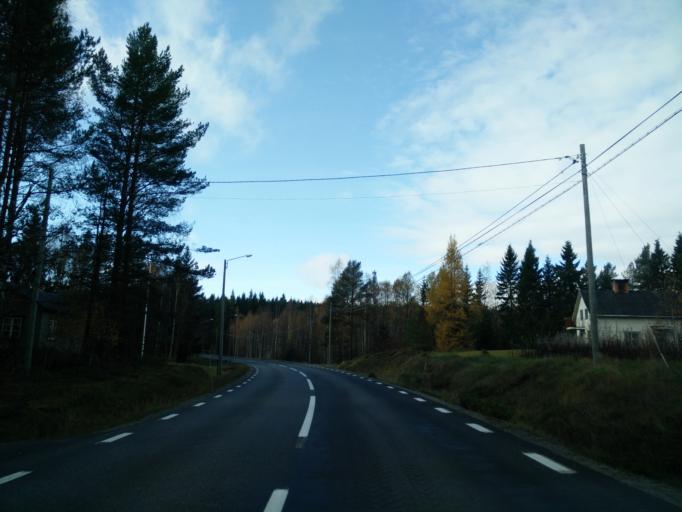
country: SE
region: Jaemtland
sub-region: Braecke Kommun
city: Braecke
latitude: 62.3971
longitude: 15.1500
